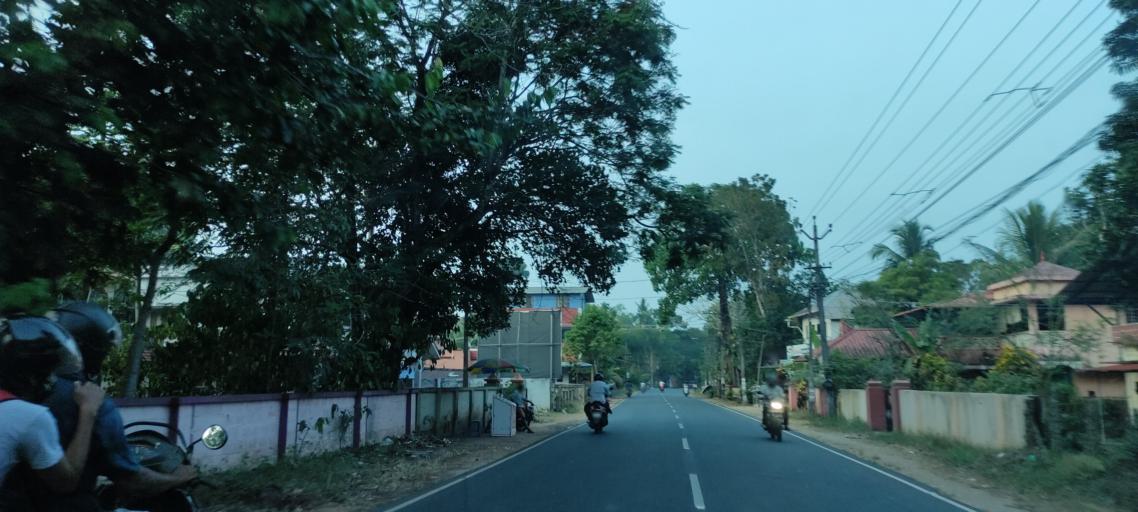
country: IN
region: Kerala
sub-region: Alappuzha
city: Mavelikara
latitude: 9.2842
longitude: 76.5312
